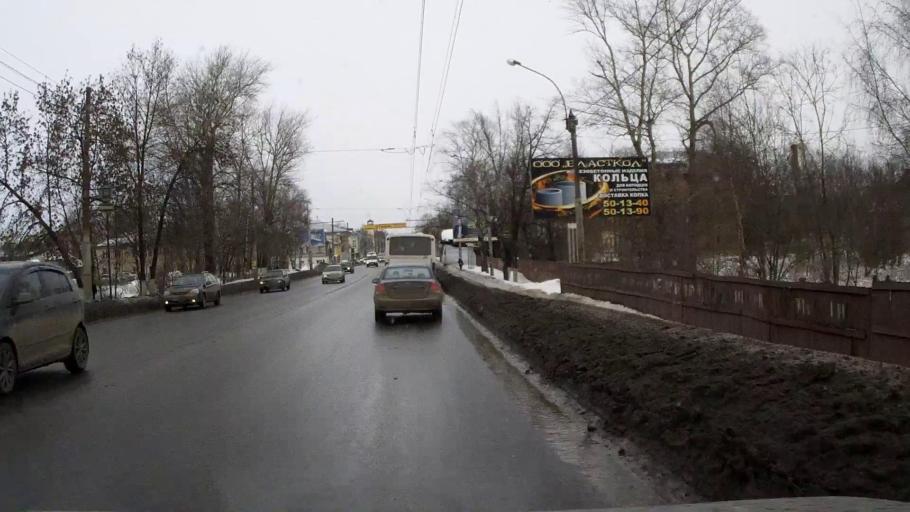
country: RU
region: Vologda
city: Vologda
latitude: 59.2249
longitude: 39.8922
